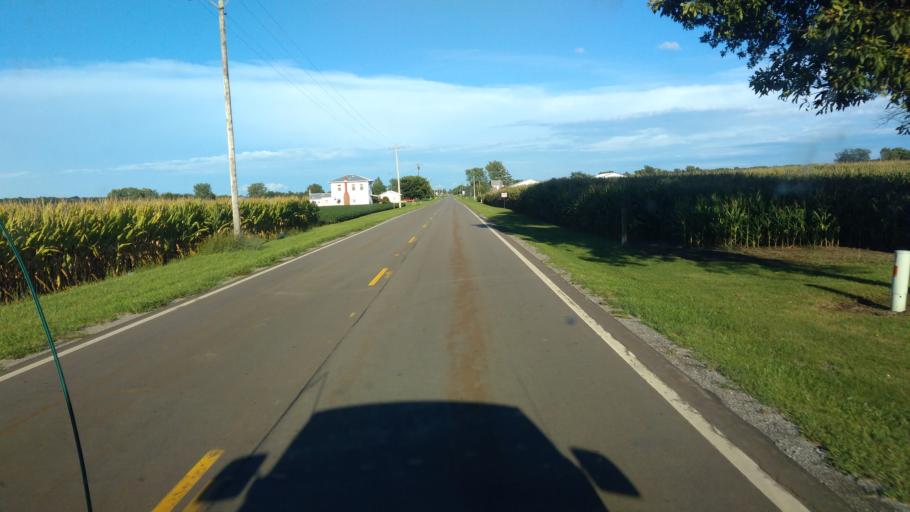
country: US
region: Ohio
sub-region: Wyandot County
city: Upper Sandusky
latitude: 40.8027
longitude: -83.3883
